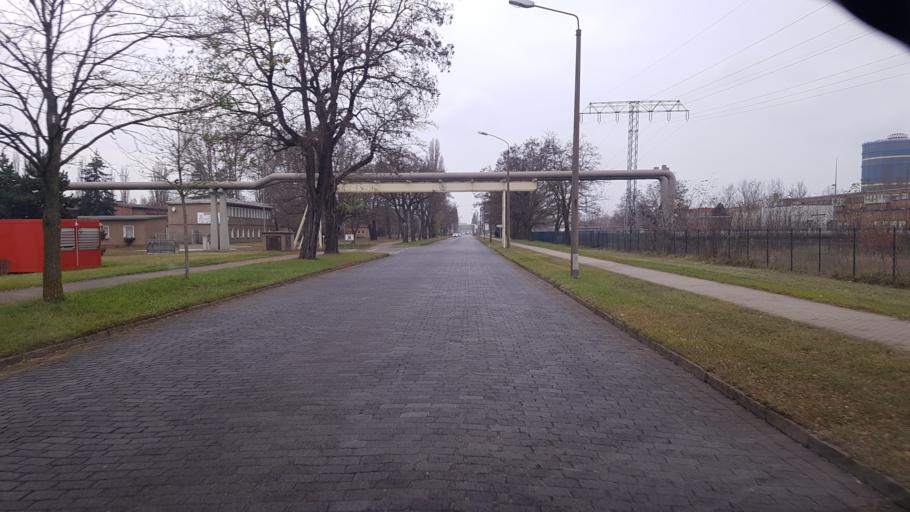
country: DE
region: Brandenburg
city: Eisenhuettenstadt
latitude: 52.1609
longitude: 14.6324
